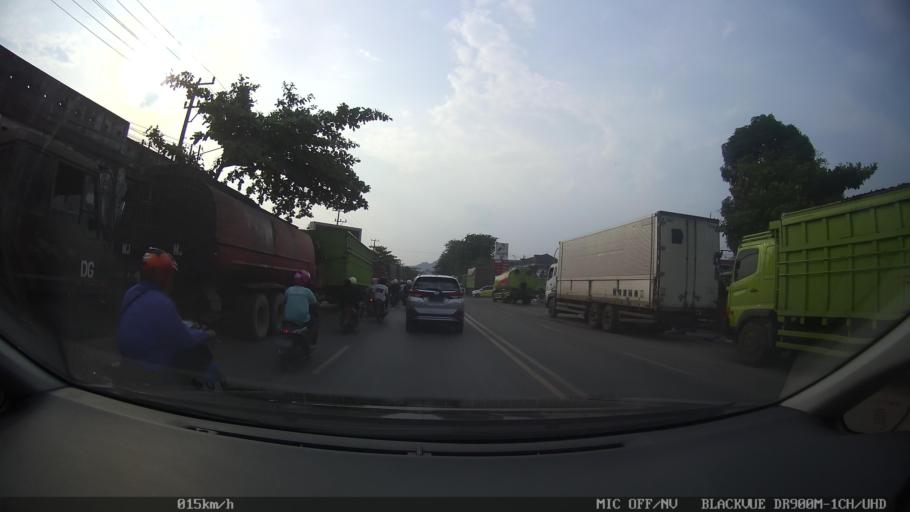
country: ID
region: Lampung
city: Panjang
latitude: -5.4499
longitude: 105.3045
